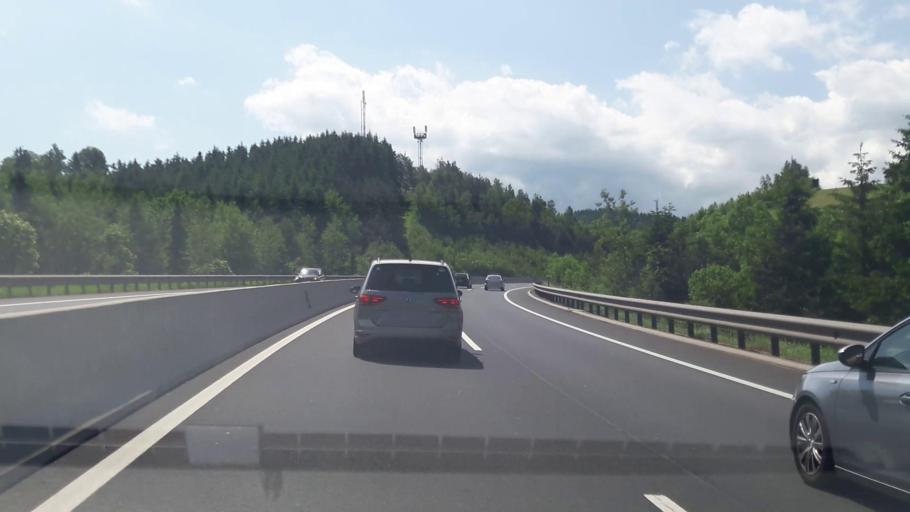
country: AT
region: Lower Austria
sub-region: Politischer Bezirk Neunkirchen
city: Zobern
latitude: 47.5056
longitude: 16.1121
